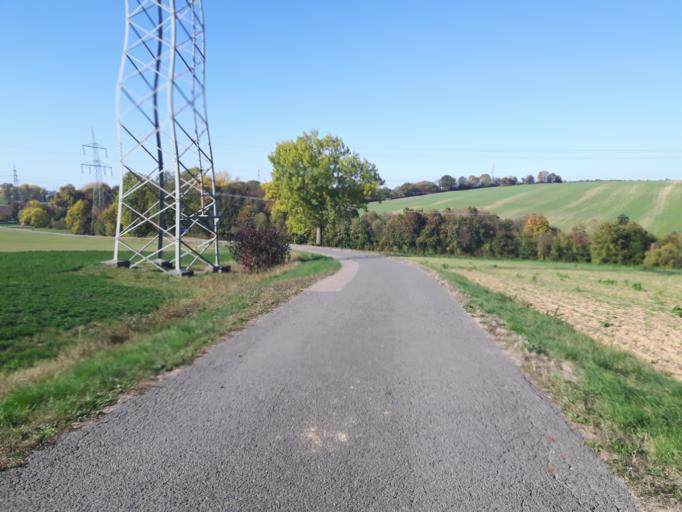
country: DE
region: Baden-Wuerttemberg
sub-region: Regierungsbezirk Stuttgart
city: Leingarten
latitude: 49.1598
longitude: 9.1543
